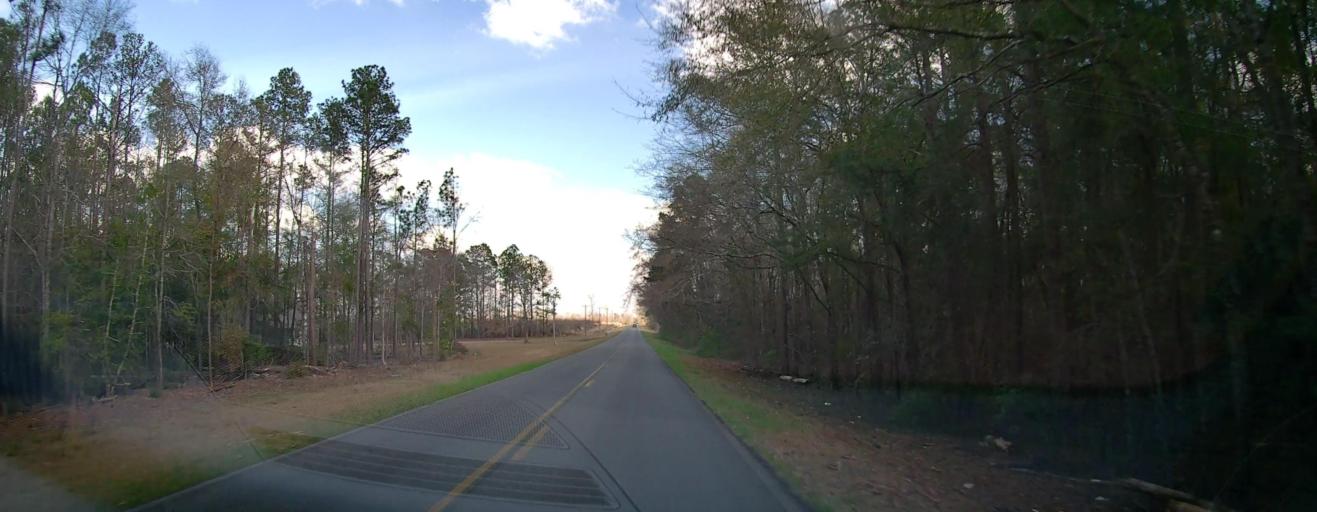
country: US
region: Georgia
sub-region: Wilkinson County
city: Irwinton
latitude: 32.6376
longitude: -83.1467
